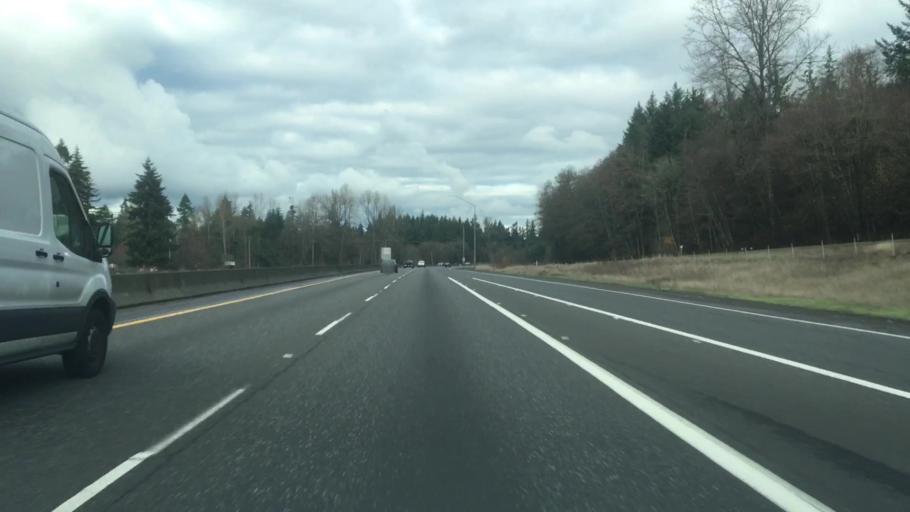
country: US
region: Washington
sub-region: Lewis County
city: Winlock
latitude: 46.3951
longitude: -122.9006
